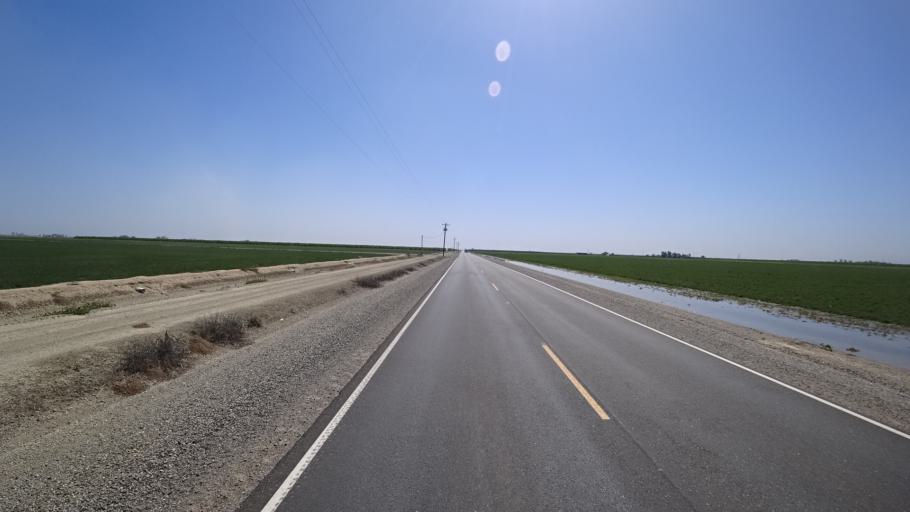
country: US
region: California
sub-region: Glenn County
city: Willows
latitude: 39.5940
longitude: -122.1372
